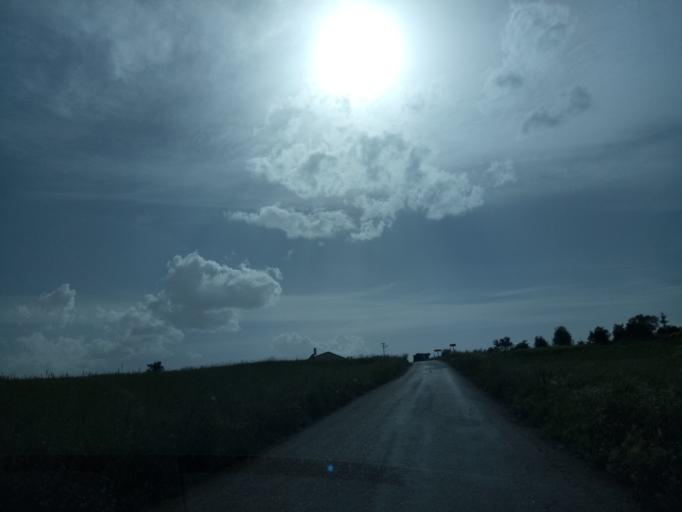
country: TR
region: Konya
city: Ahirli
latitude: 37.2842
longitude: 32.1852
